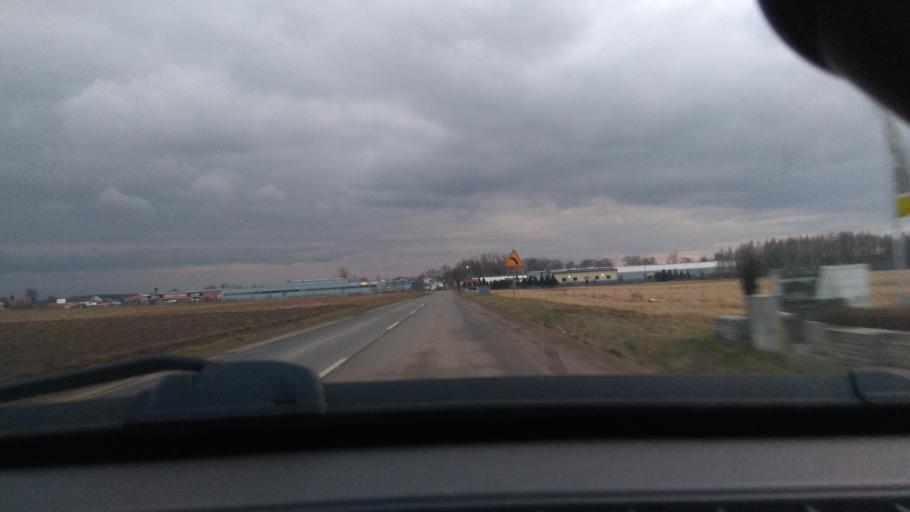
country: PL
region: Greater Poland Voivodeship
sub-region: Powiat kepinski
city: Kepno
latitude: 51.2913
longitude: 18.0061
